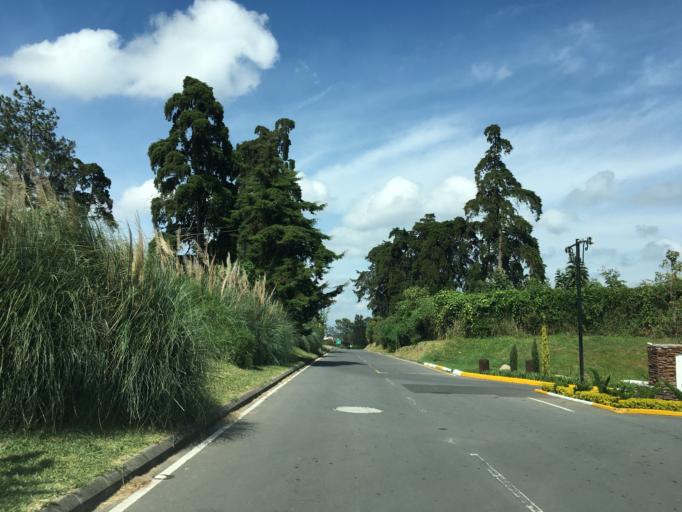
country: GT
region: Guatemala
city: Santa Catarina Pinula
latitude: 14.6039
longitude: -90.4840
